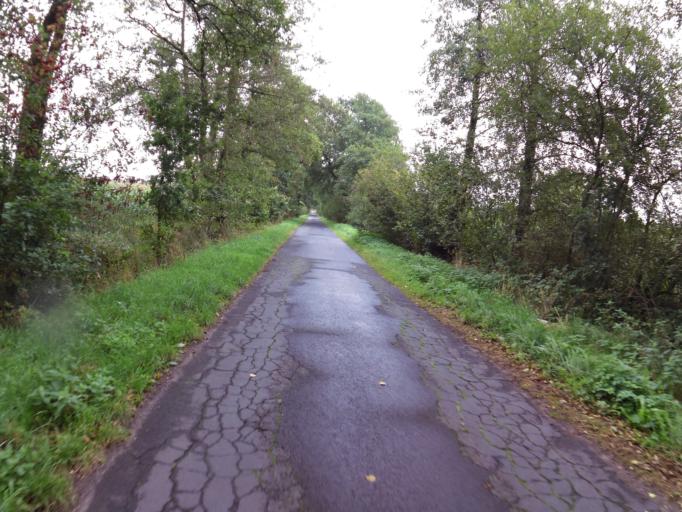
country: DE
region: Lower Saxony
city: Hamersen
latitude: 53.2630
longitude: 9.4764
